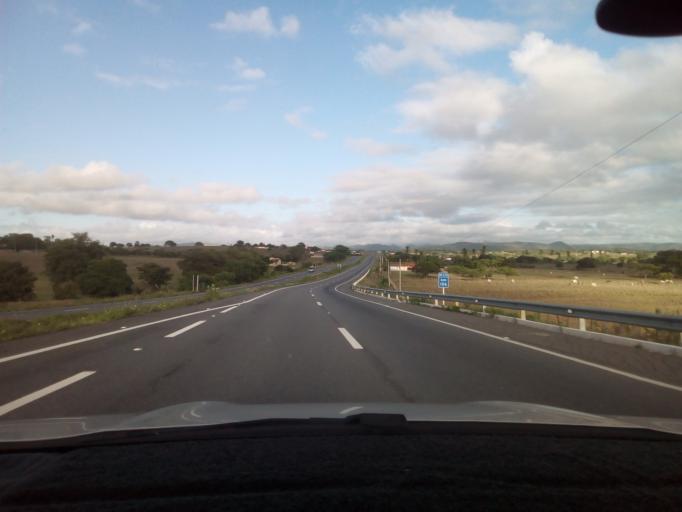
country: BR
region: Paraiba
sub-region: Inga
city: Inga
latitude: -7.2039
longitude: -35.5401
